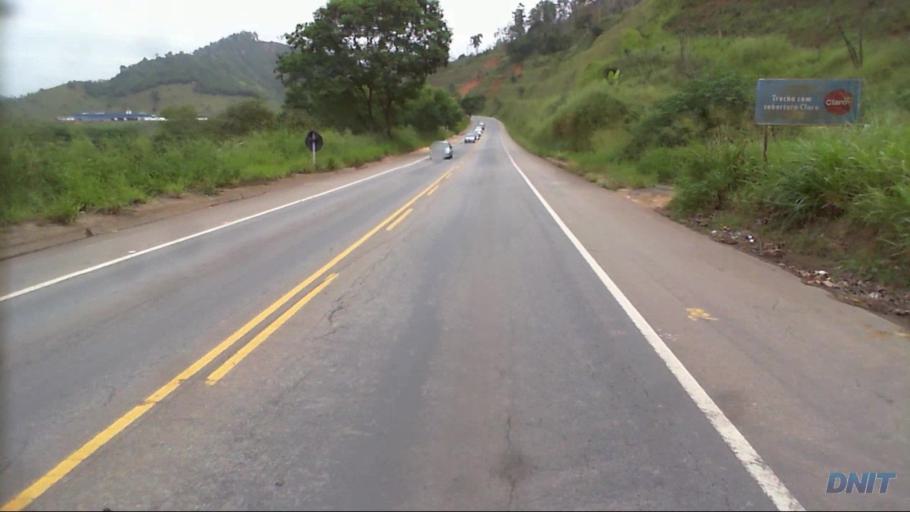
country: BR
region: Minas Gerais
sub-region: Coronel Fabriciano
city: Coronel Fabriciano
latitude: -19.5258
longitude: -42.6644
